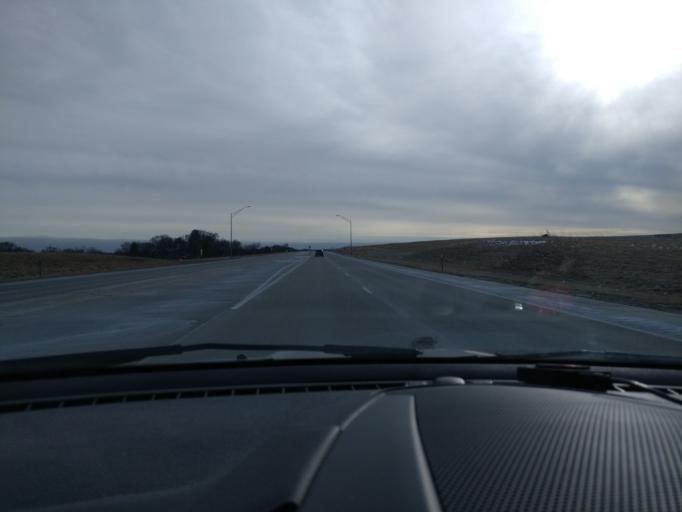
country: US
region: Nebraska
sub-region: Saunders County
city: Wahoo
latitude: 41.2211
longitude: -96.6374
